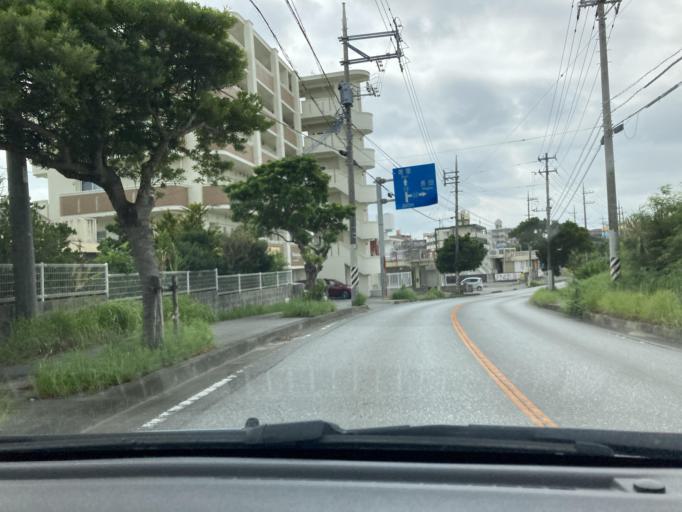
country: JP
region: Okinawa
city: Ginowan
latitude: 26.2572
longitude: 127.7763
